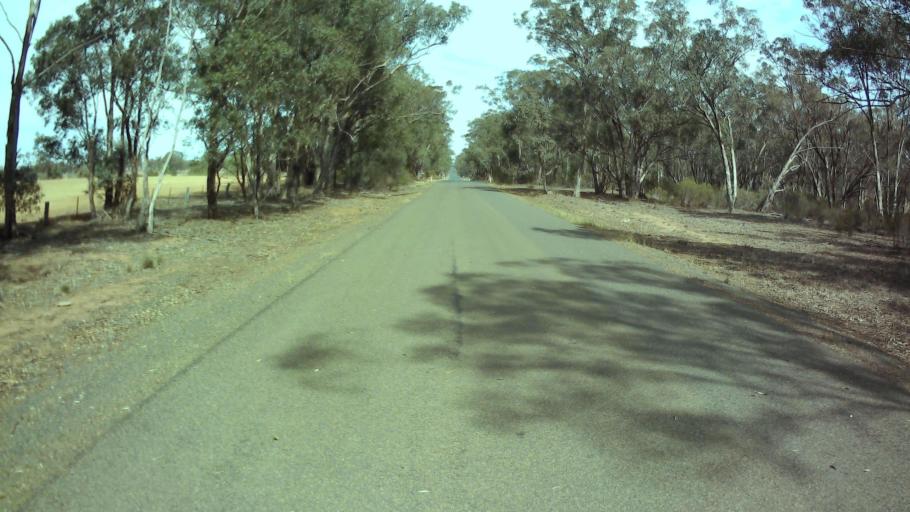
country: AU
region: New South Wales
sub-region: Weddin
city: Grenfell
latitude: -33.8079
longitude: 148.0591
